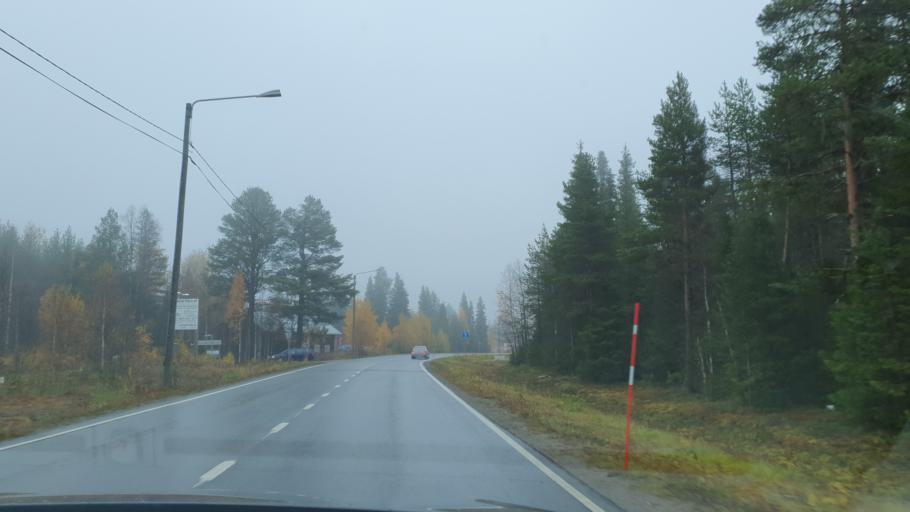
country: FI
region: Lapland
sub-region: Tunturi-Lappi
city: Kittilae
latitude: 67.6706
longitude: 24.8716
